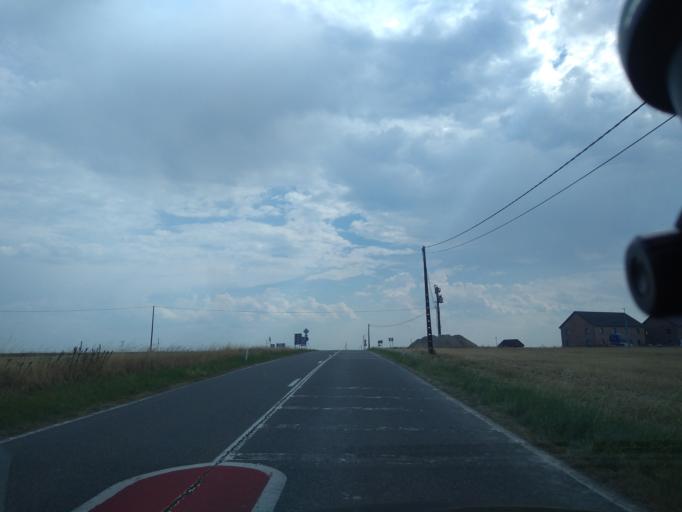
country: FR
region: Champagne-Ardenne
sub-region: Departement des Ardennes
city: Fromelennes
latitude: 50.1732
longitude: 4.9030
